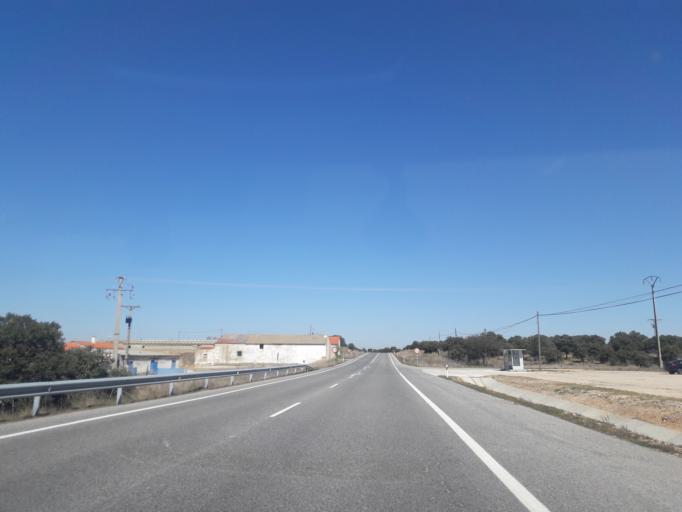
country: ES
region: Castille and Leon
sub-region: Provincia de Salamanca
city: Mozarbez
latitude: 40.8317
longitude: -5.6385
